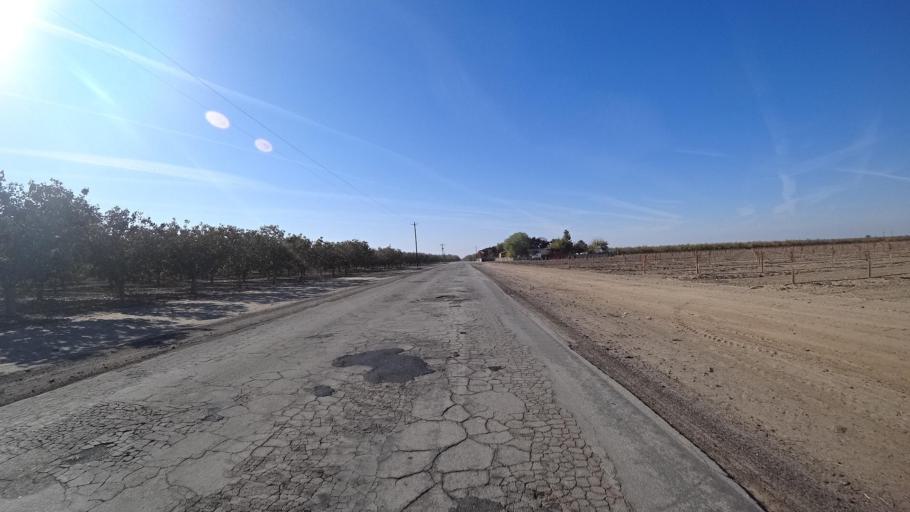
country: US
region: California
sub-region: Kern County
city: Wasco
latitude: 35.6524
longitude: -119.3459
